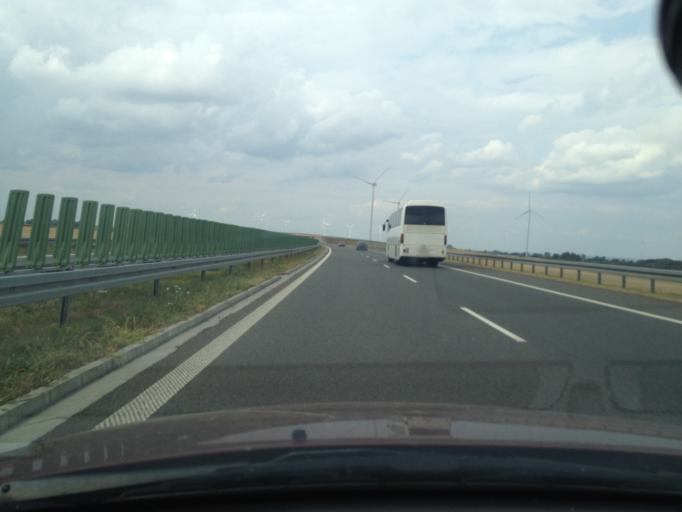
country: PL
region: West Pomeranian Voivodeship
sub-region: Powiat pyrzycki
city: Kozielice
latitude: 53.0831
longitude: 14.8497
